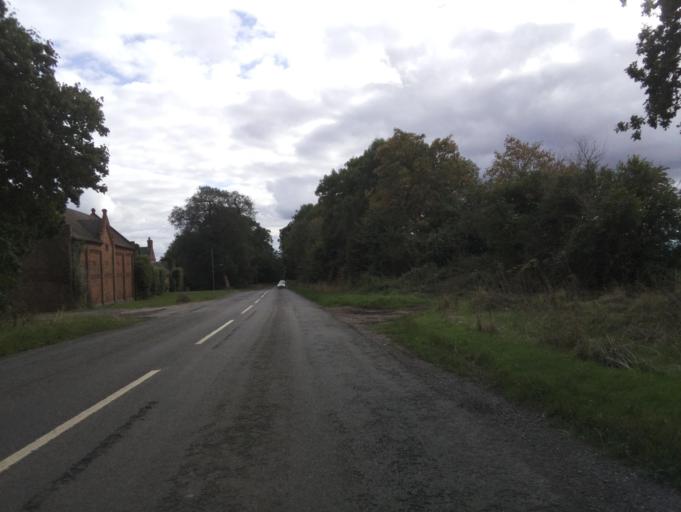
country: GB
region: England
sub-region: Nottinghamshire
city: East Leake
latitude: 52.8048
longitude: -1.1890
